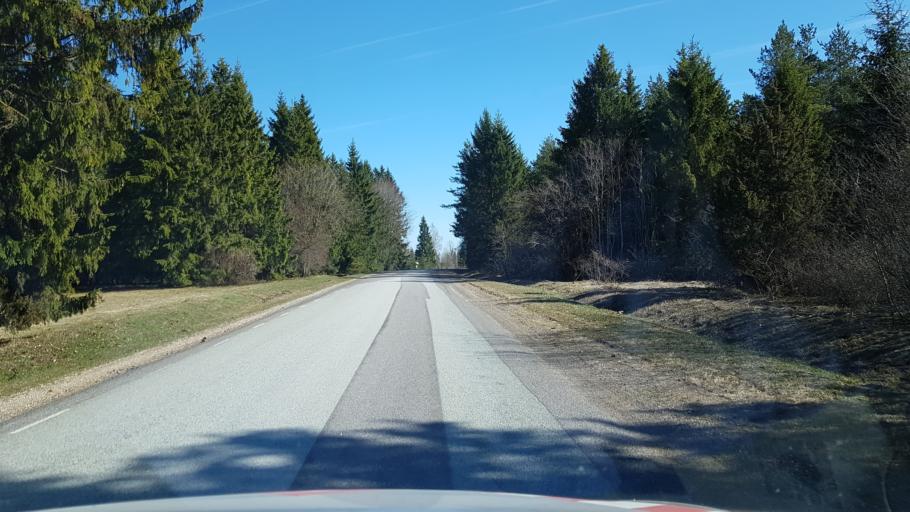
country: EE
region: Laeaene-Virumaa
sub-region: Someru vald
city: Someru
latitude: 59.3623
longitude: 26.4668
